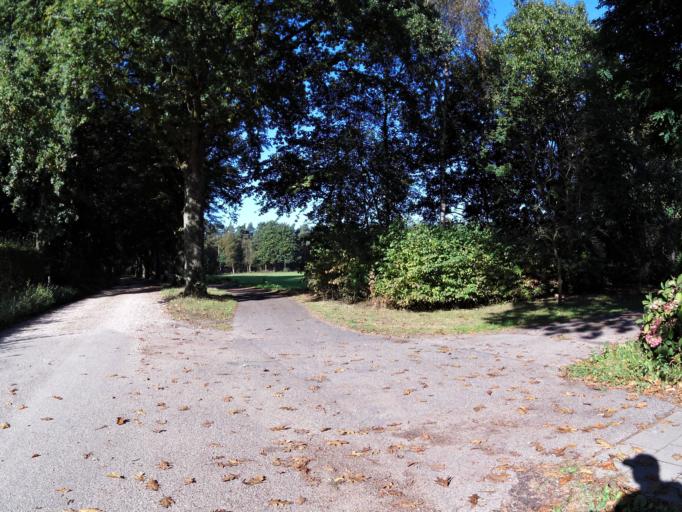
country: NL
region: Limburg
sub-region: Gemeente Venlo
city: Arcen
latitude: 51.4552
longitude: 6.1982
